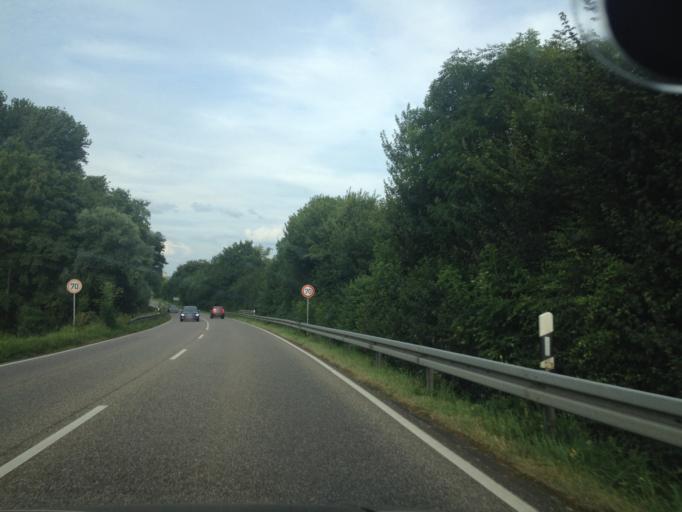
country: DE
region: Baden-Wuerttemberg
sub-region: Regierungsbezirk Stuttgart
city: Leingarten
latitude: 49.1449
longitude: 9.0880
